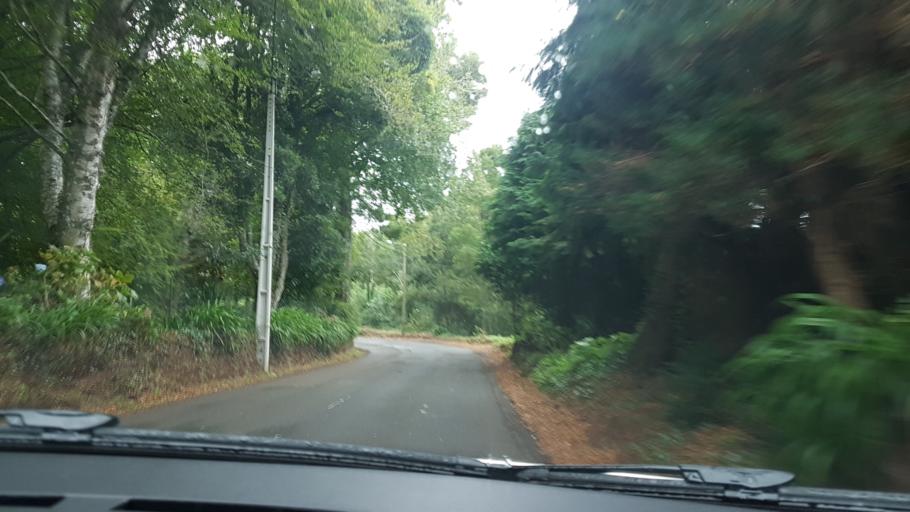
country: PT
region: Madeira
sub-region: Santa Cruz
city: Santa Cruz
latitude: 32.7248
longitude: -16.8164
